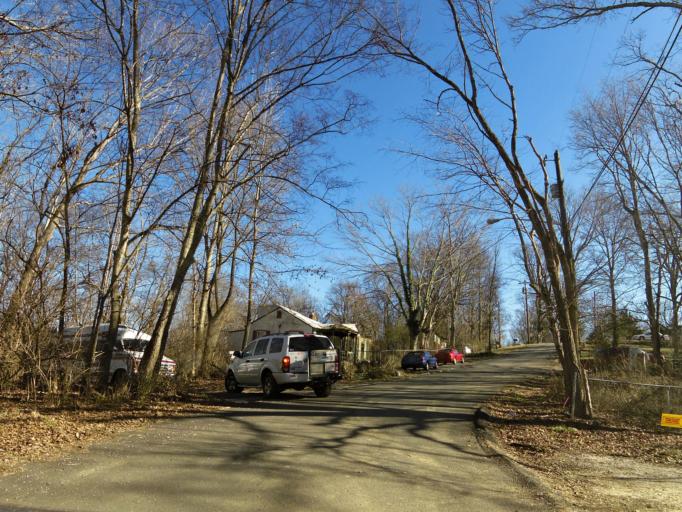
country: US
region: Tennessee
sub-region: Knox County
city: Knoxville
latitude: 35.9402
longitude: -83.8710
